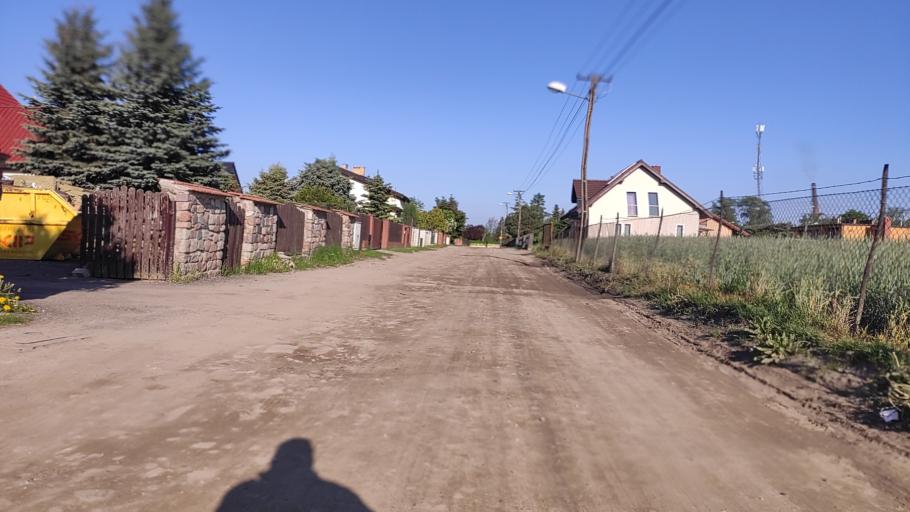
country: PL
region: Greater Poland Voivodeship
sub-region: Powiat poznanski
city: Kostrzyn
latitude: 52.4021
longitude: 17.1662
